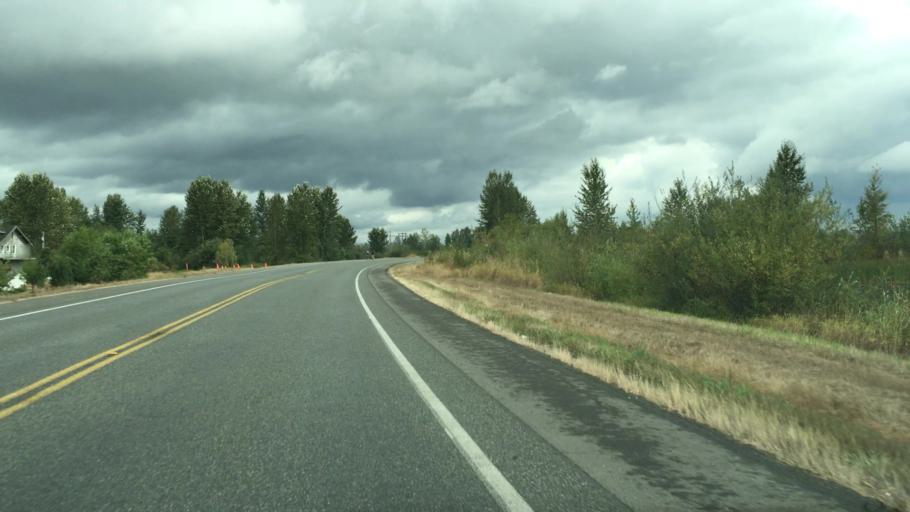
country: US
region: Washington
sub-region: Snohomish County
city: Fobes Hill
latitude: 47.9324
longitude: -122.1721
